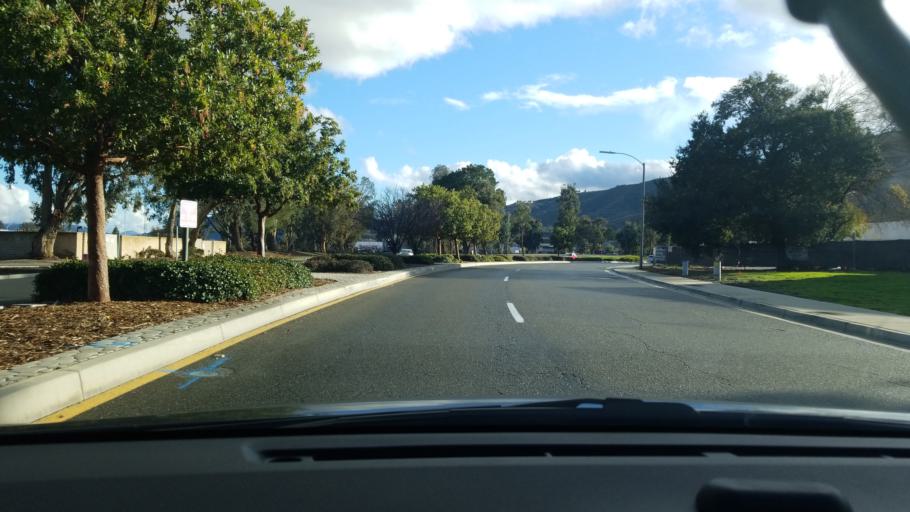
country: US
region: California
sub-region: Riverside County
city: Temecula
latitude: 33.5013
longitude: -117.1567
